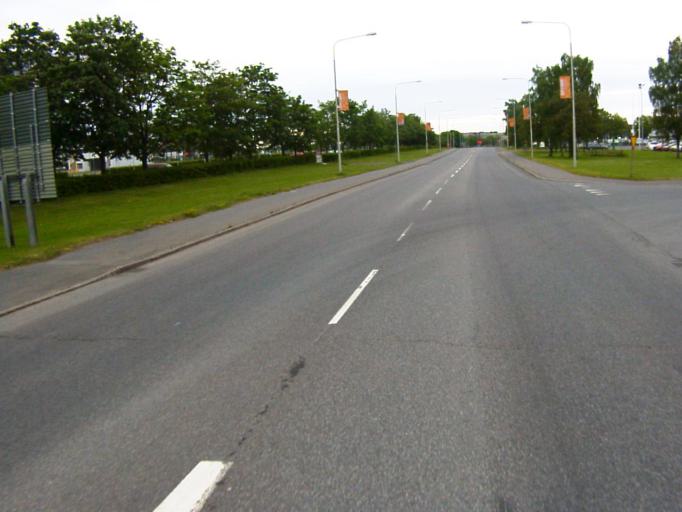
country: SE
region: Skane
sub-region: Kristianstads Kommun
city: Kristianstad
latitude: 56.0279
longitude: 14.1726
